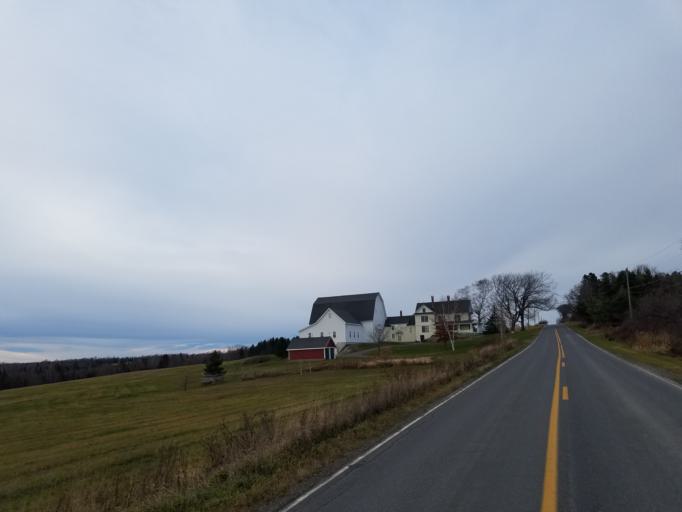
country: US
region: Maine
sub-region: Aroostook County
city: Caribou
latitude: 46.8612
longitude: -68.2085
